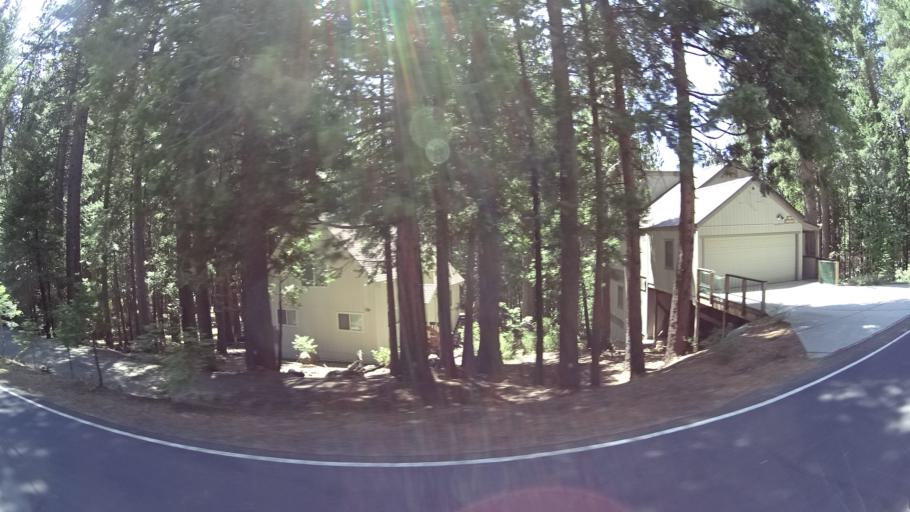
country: US
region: California
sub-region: Calaveras County
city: Arnold
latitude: 38.3138
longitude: -120.2563
